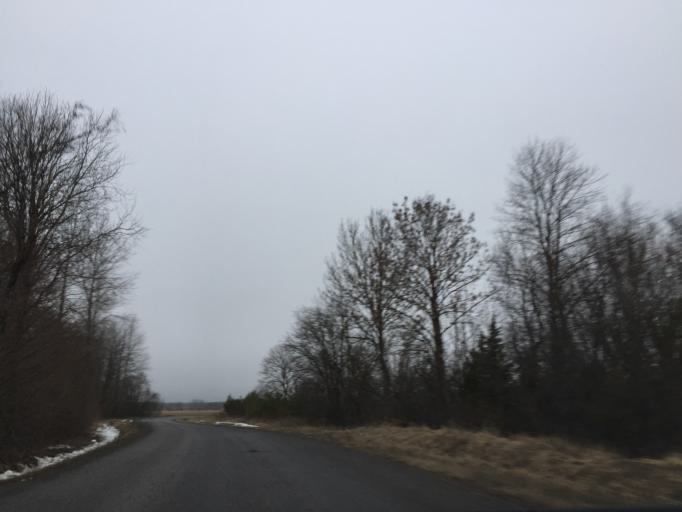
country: EE
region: Laeaene
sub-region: Lihula vald
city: Lihula
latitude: 58.6452
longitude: 23.6238
